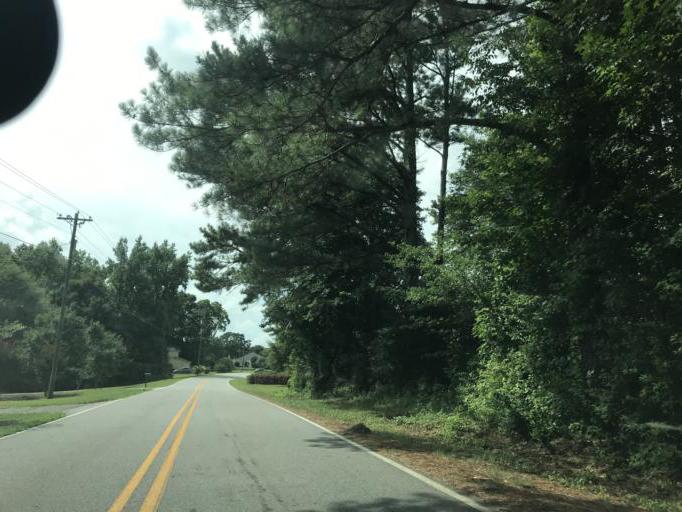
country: US
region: Georgia
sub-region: Forsyth County
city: Cumming
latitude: 34.2321
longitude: -84.2433
